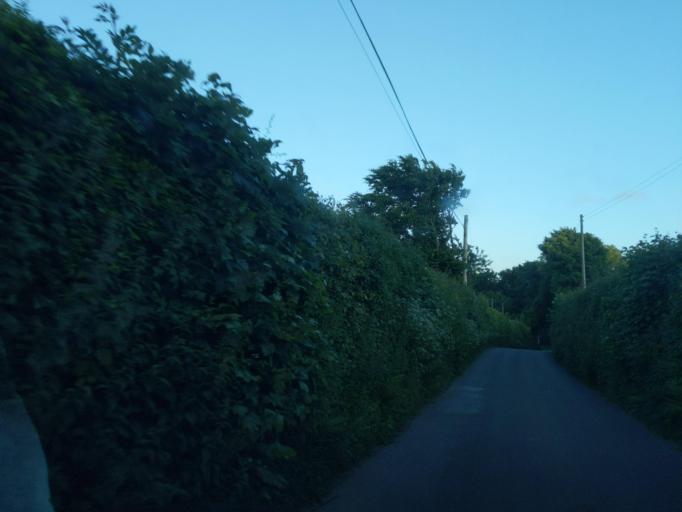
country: GB
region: England
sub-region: Devon
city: Great Torrington
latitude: 50.9350
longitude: -4.1523
